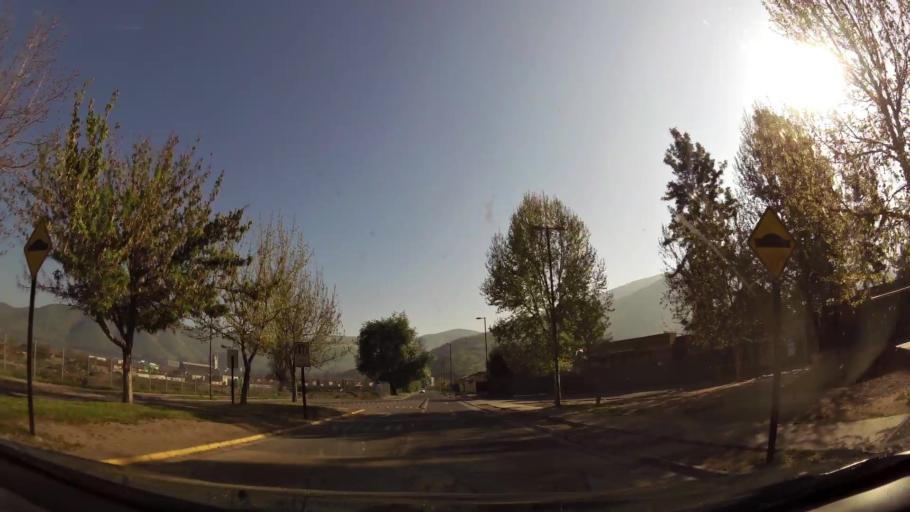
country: CL
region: Santiago Metropolitan
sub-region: Provincia de Chacabuco
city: Chicureo Abajo
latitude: -33.3573
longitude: -70.6636
